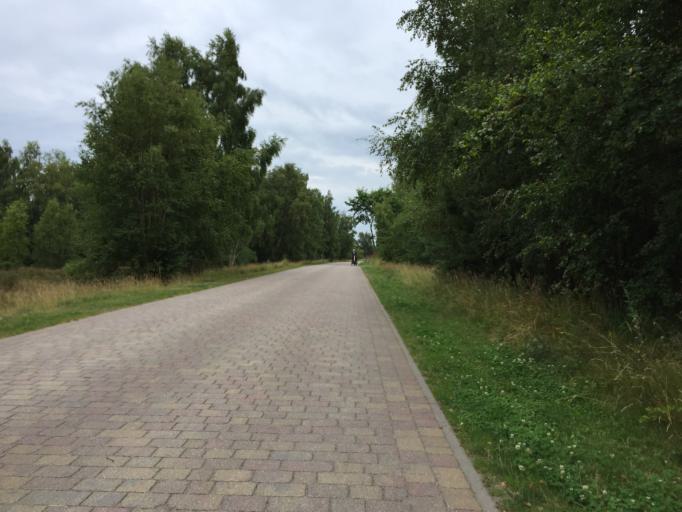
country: DE
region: Mecklenburg-Vorpommern
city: Hiddensee
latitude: 54.5458
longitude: 13.1054
